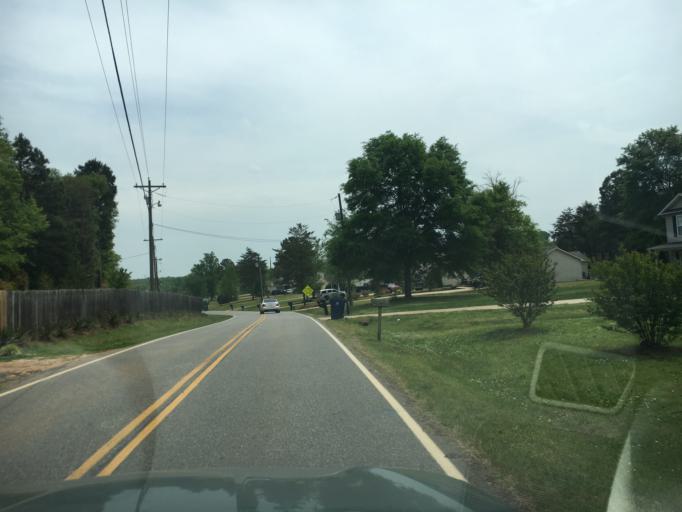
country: US
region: South Carolina
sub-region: Spartanburg County
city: Wellford
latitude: 34.9895
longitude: -82.1004
